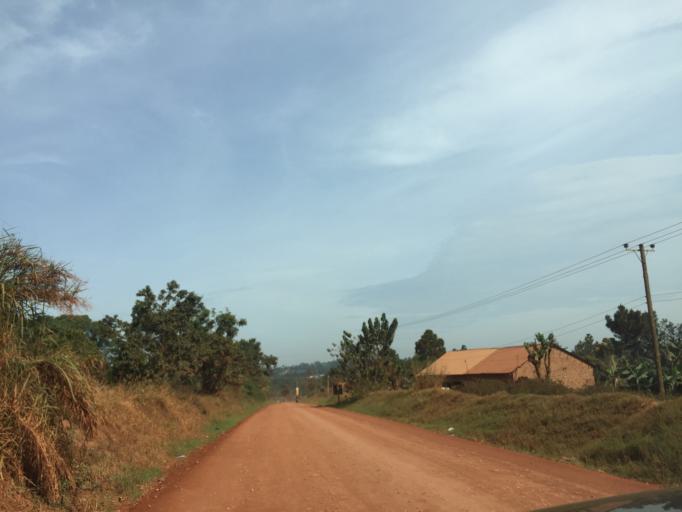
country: UG
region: Central Region
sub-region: Wakiso District
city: Kireka
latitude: 0.4485
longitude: 32.5785
